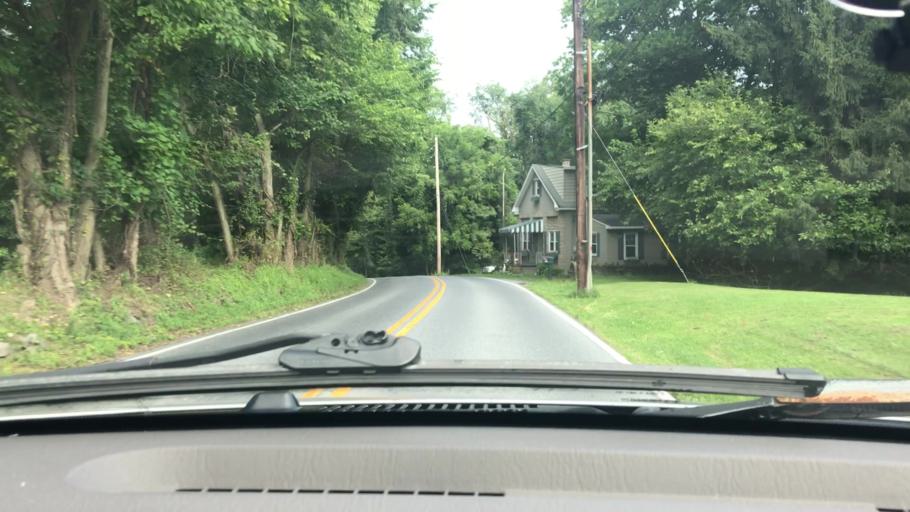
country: US
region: Pennsylvania
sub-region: Dauphin County
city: Highspire
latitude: 40.2073
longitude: -76.7616
